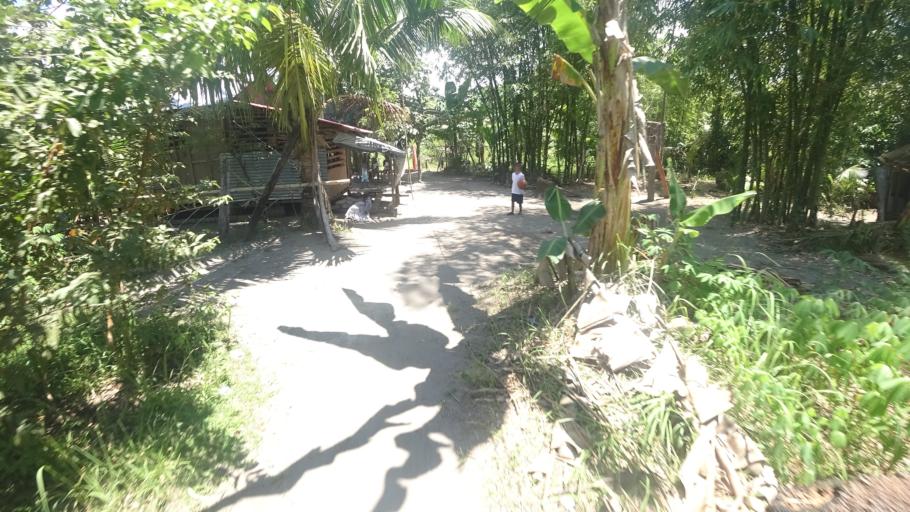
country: PH
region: Eastern Visayas
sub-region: Province of Leyte
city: Liberty
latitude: 10.8867
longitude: 125.0054
